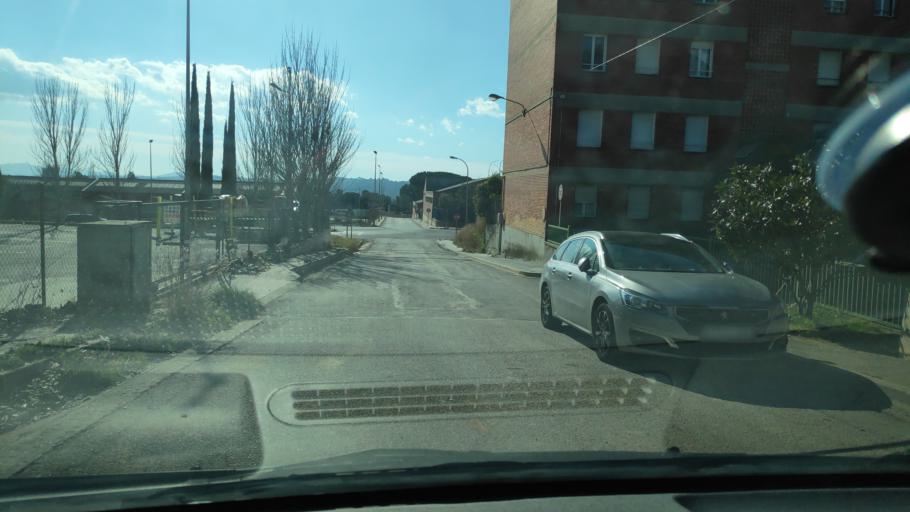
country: ES
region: Catalonia
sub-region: Provincia de Barcelona
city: Sant Quirze del Valles
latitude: 41.5554
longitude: 2.0593
